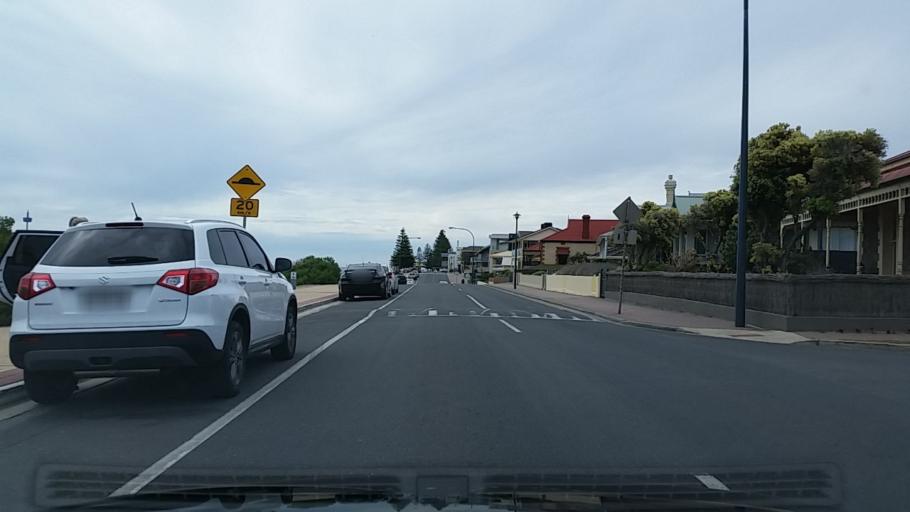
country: AU
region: South Australia
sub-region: Adelaide
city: Brighton
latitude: -35.0206
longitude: 138.5158
